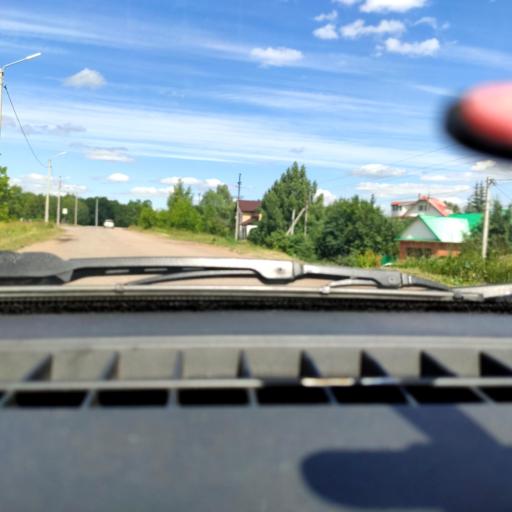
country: RU
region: Bashkortostan
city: Ufa
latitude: 54.6564
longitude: 56.0612
